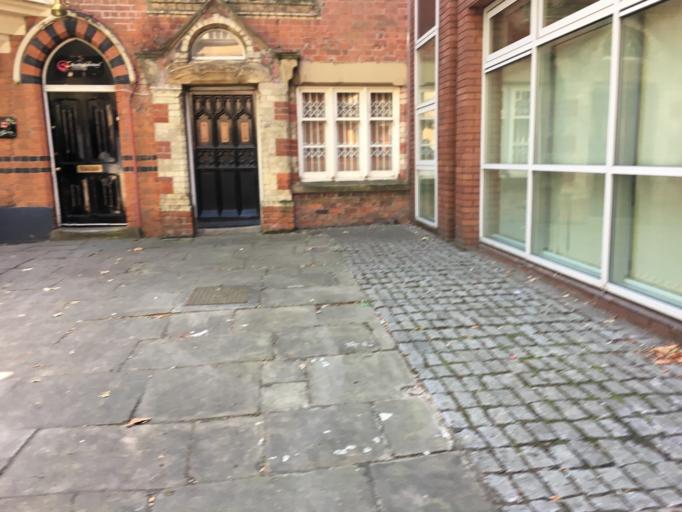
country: GB
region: England
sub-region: City of Kingston upon Hull
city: Hull
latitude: 53.7435
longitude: -0.3325
